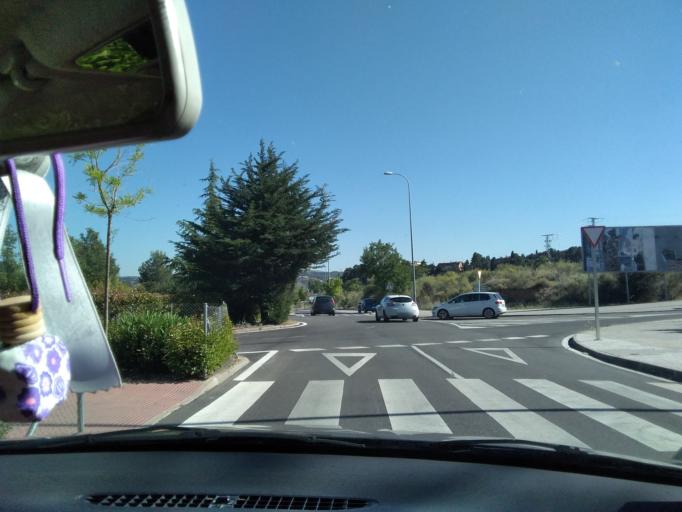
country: ES
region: Castille-La Mancha
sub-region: Province of Toledo
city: Toledo
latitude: 39.8896
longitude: -4.0555
